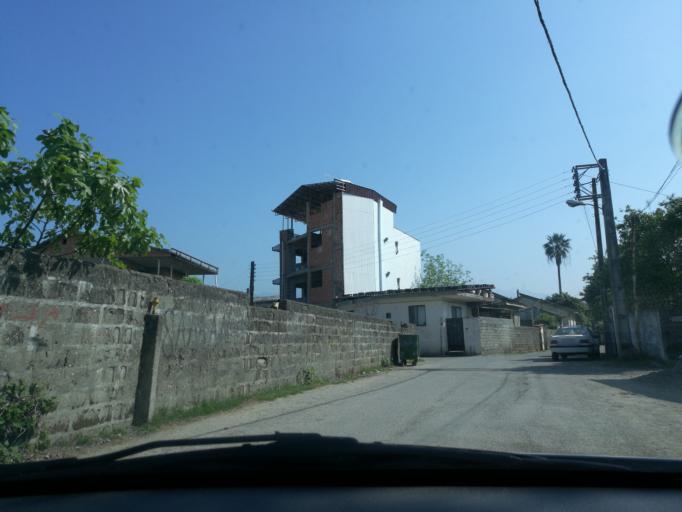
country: IR
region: Mazandaran
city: Chalus
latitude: 36.6689
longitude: 51.4321
